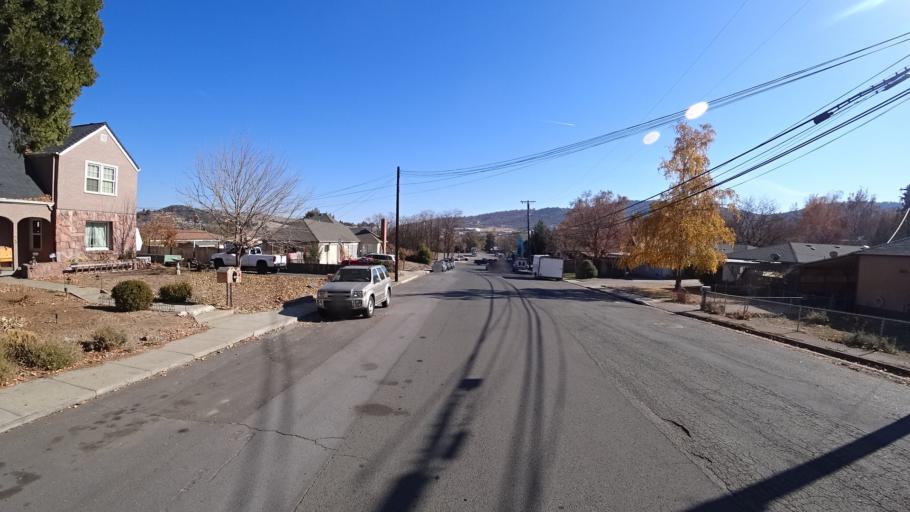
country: US
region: California
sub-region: Siskiyou County
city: Yreka
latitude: 41.7391
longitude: -122.6347
